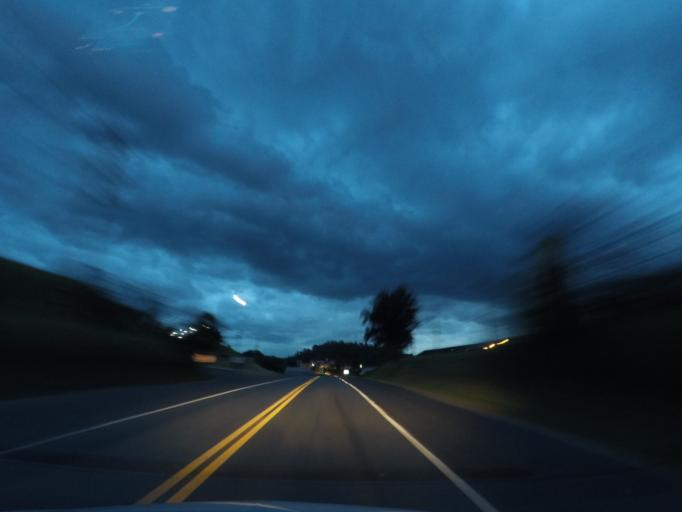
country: BR
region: Sao Paulo
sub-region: Vinhedo
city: Vinhedo
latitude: -23.0602
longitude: -47.0289
